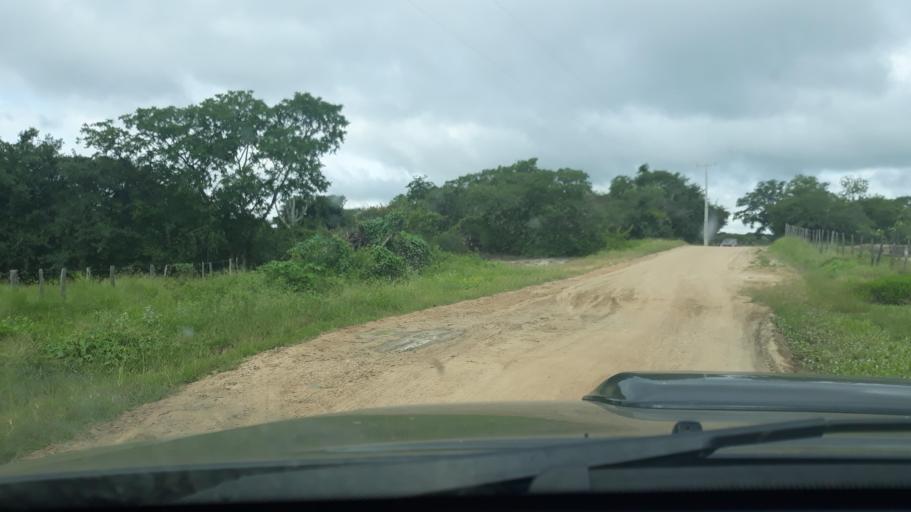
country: BR
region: Bahia
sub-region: Riacho De Santana
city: Riacho de Santana
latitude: -13.9002
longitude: -42.8807
